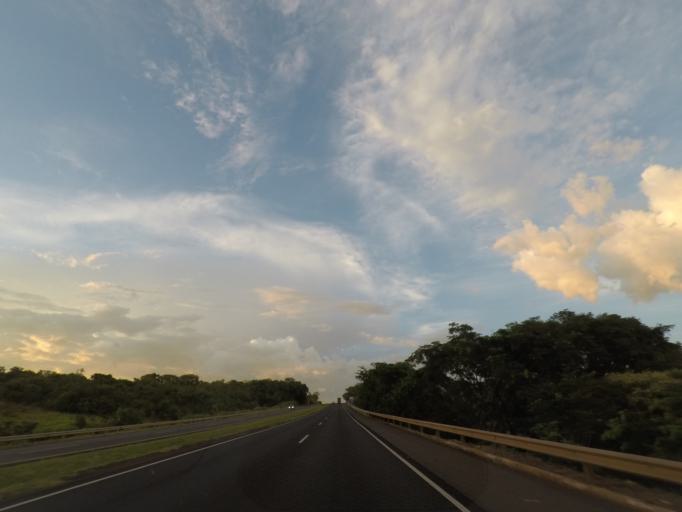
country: BR
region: Minas Gerais
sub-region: Uberaba
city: Uberaba
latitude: -19.6887
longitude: -47.9913
